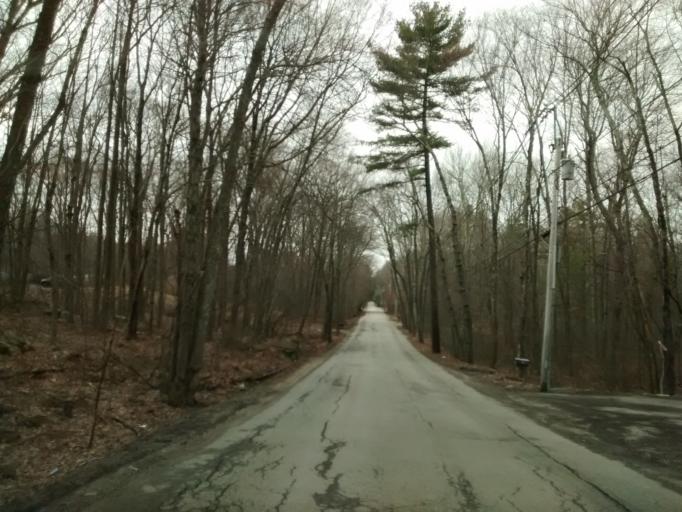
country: US
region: Massachusetts
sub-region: Worcester County
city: Douglas
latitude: 42.0475
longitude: -71.7281
